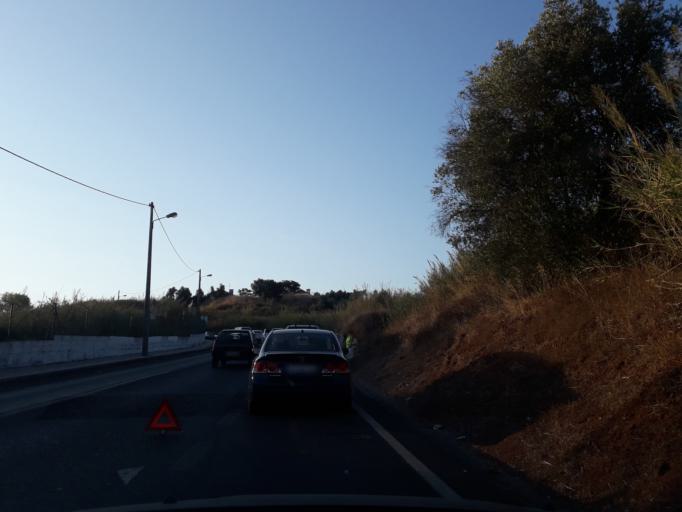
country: PT
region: Lisbon
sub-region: Odivelas
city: Pontinha
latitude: 38.7706
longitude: -9.2004
